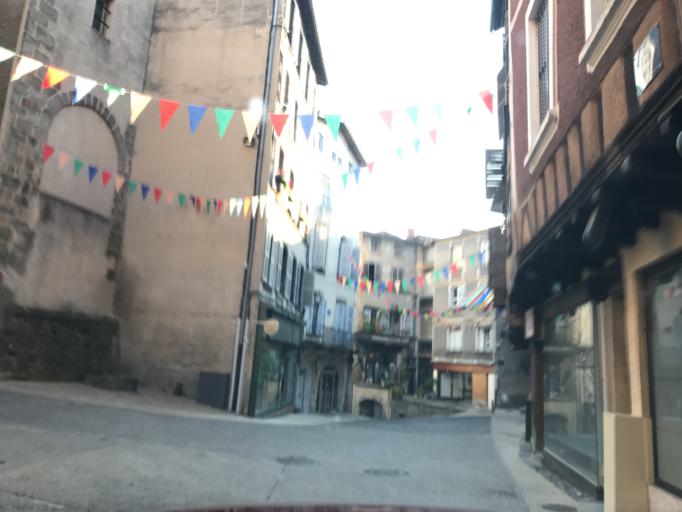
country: FR
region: Auvergne
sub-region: Departement du Puy-de-Dome
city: Thiers
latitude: 45.8542
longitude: 3.5482
